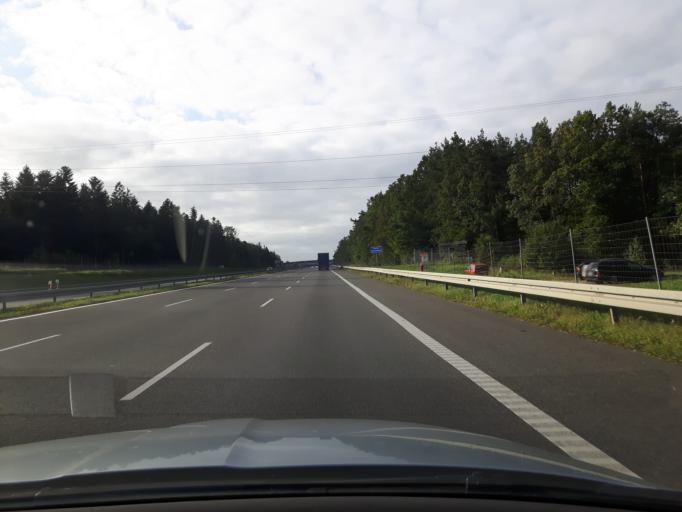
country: PL
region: Swietokrzyskie
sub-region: Powiat skarzyski
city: Suchedniow
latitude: 51.0839
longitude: 20.8360
